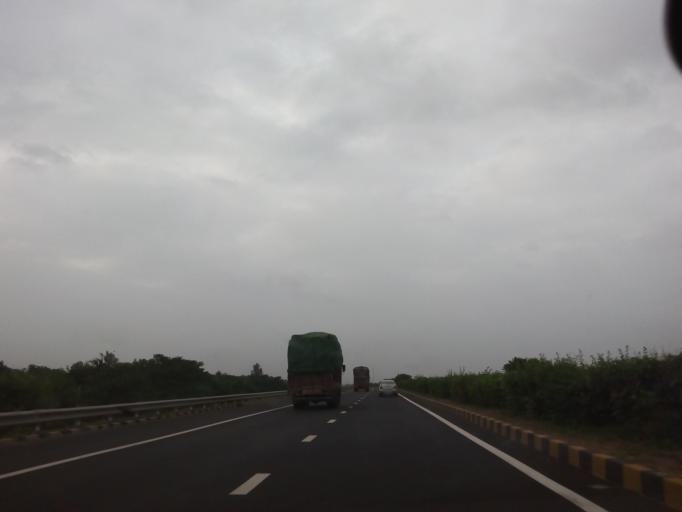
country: IN
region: Gujarat
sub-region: Kheda
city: Chaklasi
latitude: 22.6724
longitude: 72.9136
